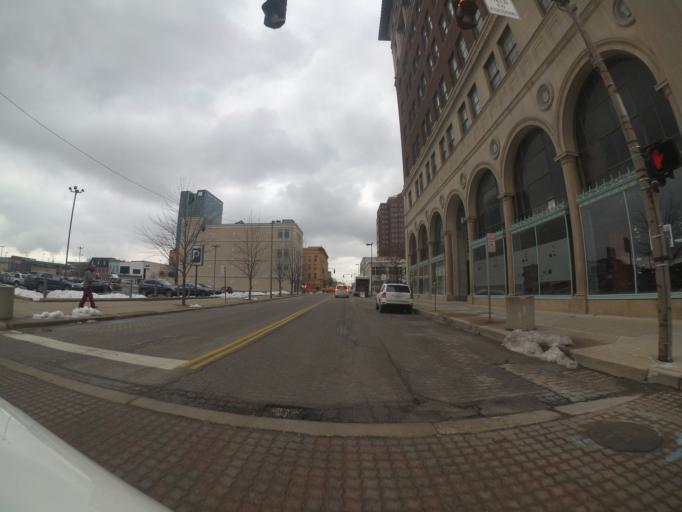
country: US
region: Ohio
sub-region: Lucas County
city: Toledo
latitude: 41.6536
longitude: -83.5358
